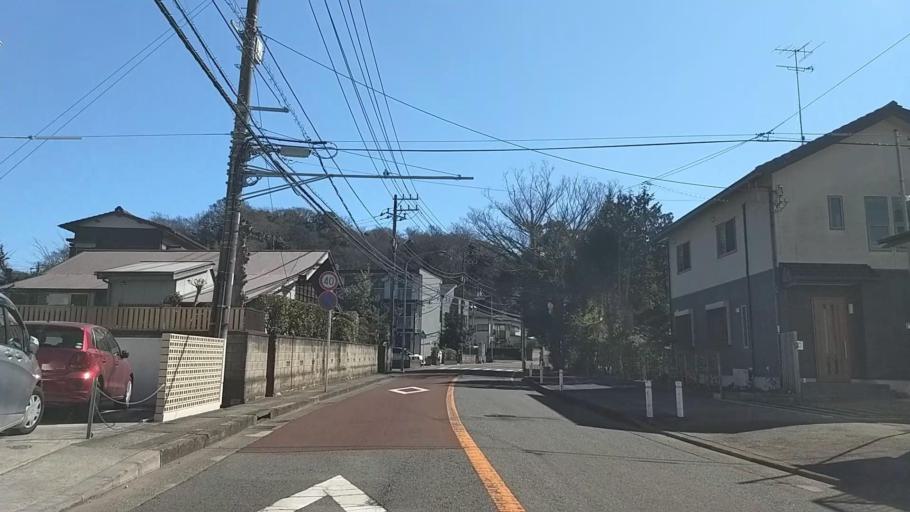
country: JP
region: Kanagawa
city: Kamakura
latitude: 35.3216
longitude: 139.5273
